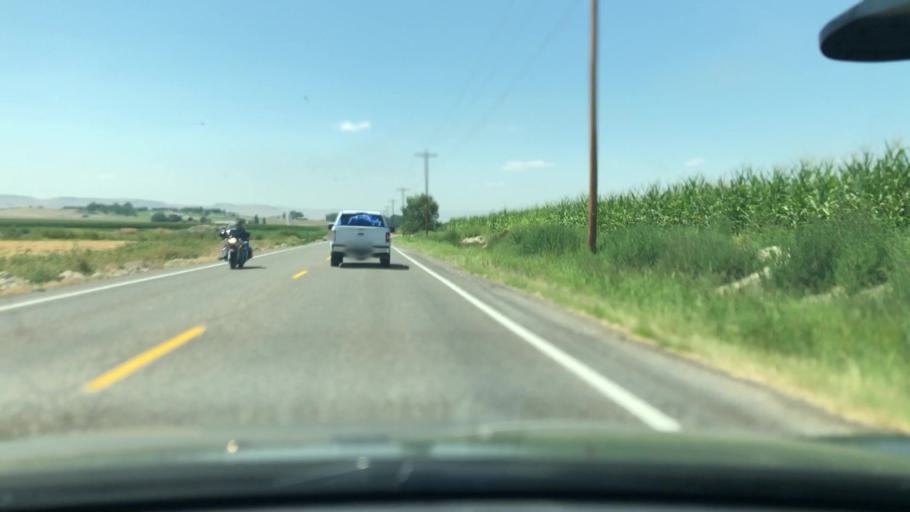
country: US
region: Idaho
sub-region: Owyhee County
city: Marsing
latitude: 43.5452
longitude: -116.8767
